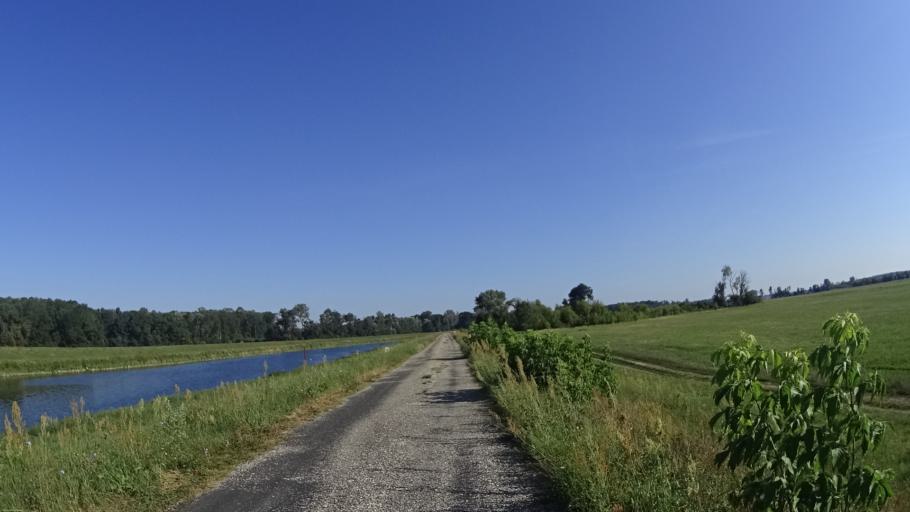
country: CZ
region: South Moravian
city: Tvrdonice
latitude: 48.7238
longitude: 17.0143
